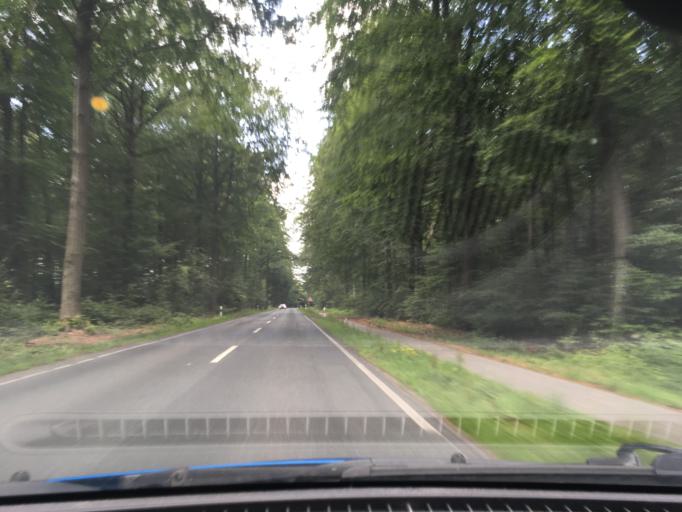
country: DE
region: Lower Saxony
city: Bendestorf
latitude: 53.3466
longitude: 9.9410
